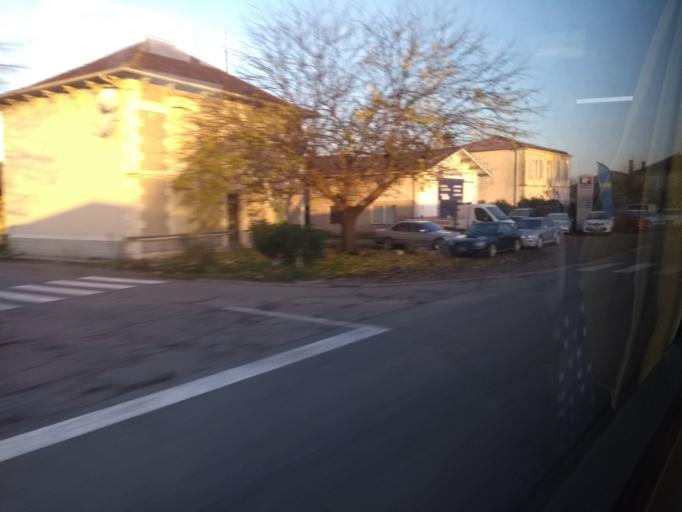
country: FR
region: Aquitaine
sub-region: Departement de la Gironde
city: Le Barp
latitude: 44.6038
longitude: -0.7706
